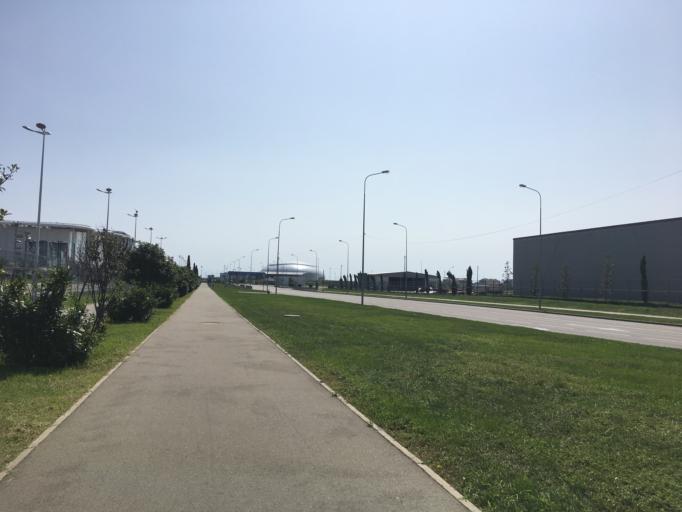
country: RU
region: Krasnodarskiy
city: Adler
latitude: 43.4158
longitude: 39.9476
